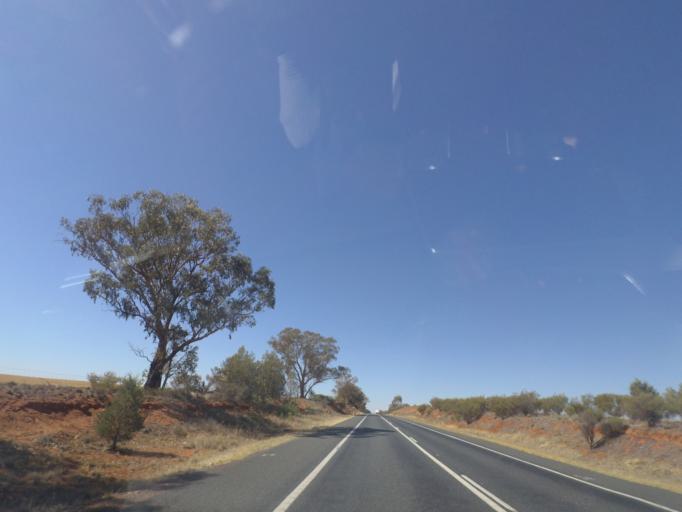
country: AU
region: New South Wales
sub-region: Bland
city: West Wyalong
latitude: -34.1782
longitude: 147.1138
